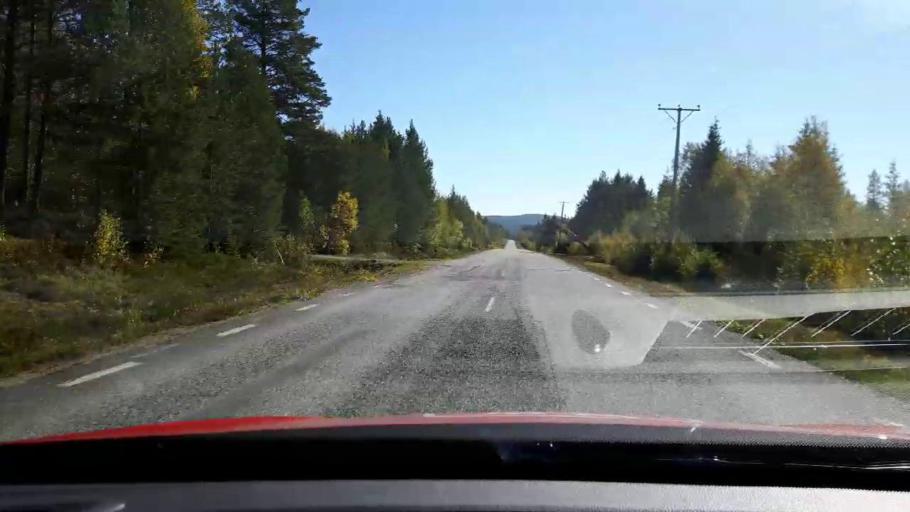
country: SE
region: Jaemtland
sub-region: Harjedalens Kommun
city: Sveg
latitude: 62.3032
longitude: 14.0573
